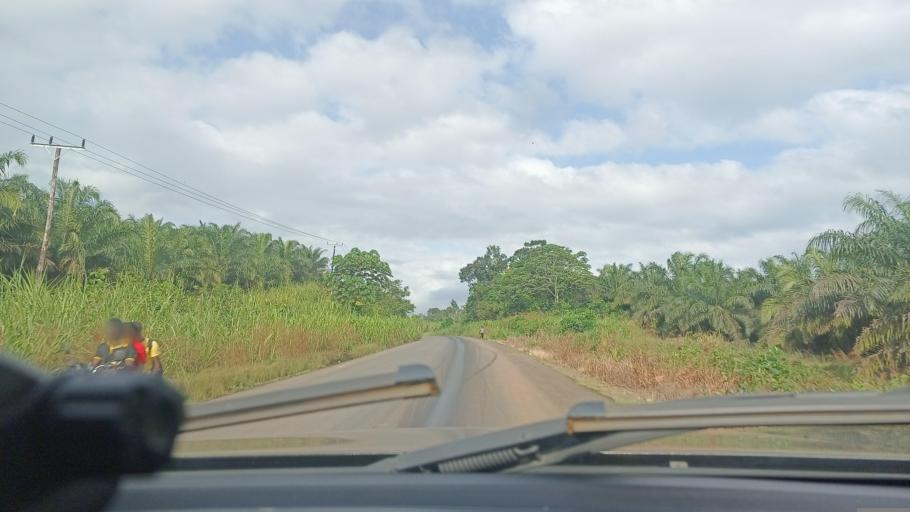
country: LR
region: Bomi
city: Tubmanburg
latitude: 6.7314
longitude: -10.9926
